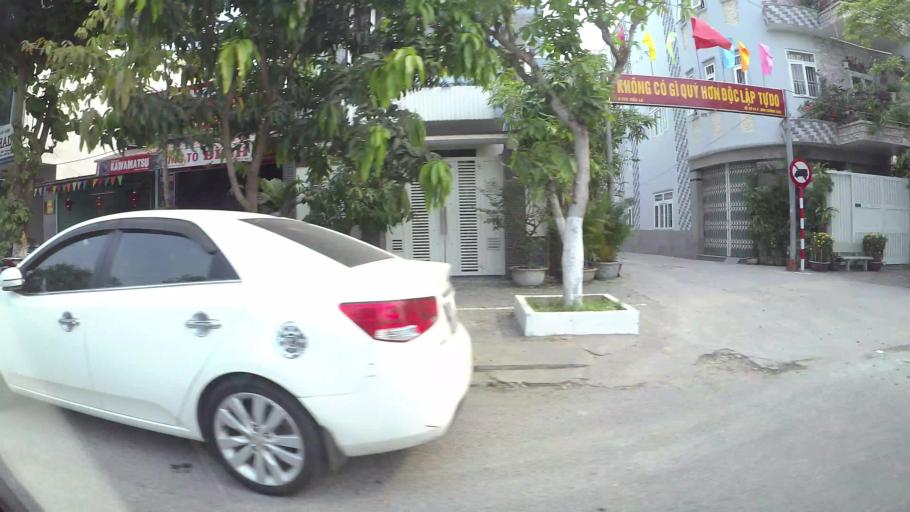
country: VN
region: Da Nang
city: Da Nang
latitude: 16.0444
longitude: 108.2140
